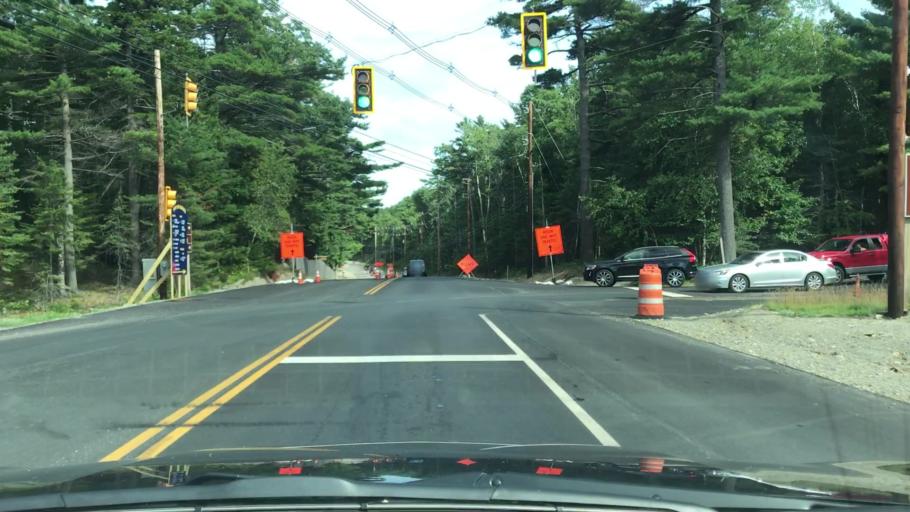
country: US
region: Maine
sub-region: Hancock County
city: Bar Harbor
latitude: 44.4104
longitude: -68.2462
